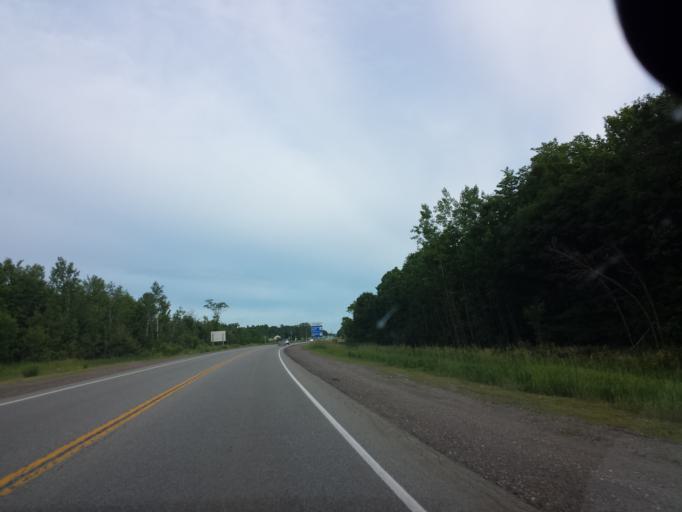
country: CA
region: Ontario
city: Arnprior
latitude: 45.4392
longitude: -76.4995
